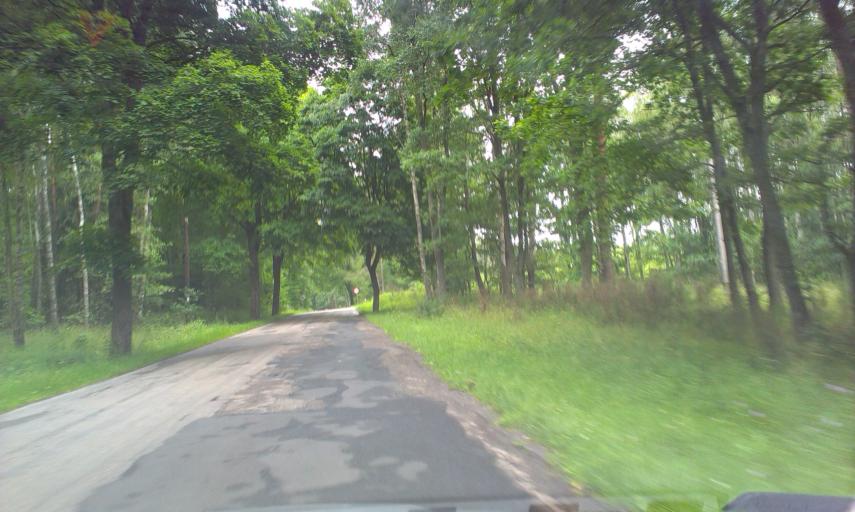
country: PL
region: West Pomeranian Voivodeship
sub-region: Powiat szczecinecki
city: Barwice
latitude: 53.6689
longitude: 16.3413
